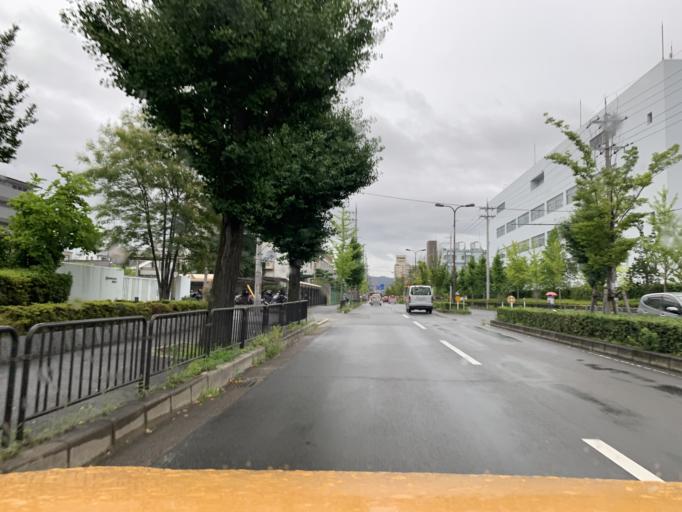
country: JP
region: Kyoto
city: Kyoto
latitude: 35.0110
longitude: 135.7280
